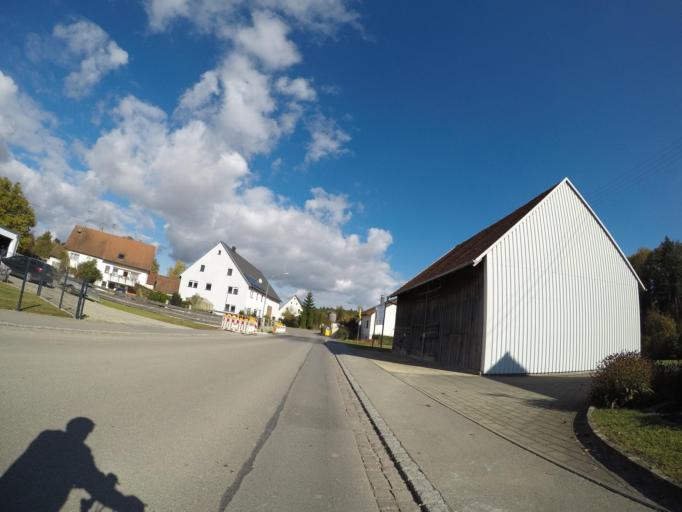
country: DE
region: Baden-Wuerttemberg
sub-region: Tuebingen Region
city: Oberstadion
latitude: 48.1701
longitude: 9.6883
